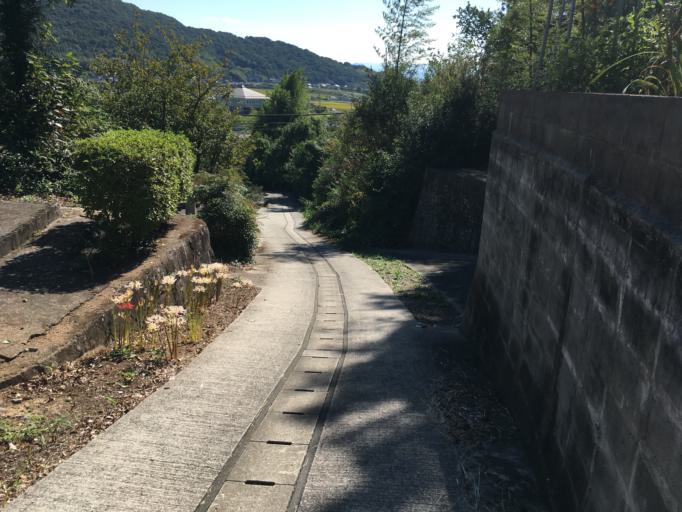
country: JP
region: Kumamoto
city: Kumamoto
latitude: 32.7930
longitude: 130.6677
